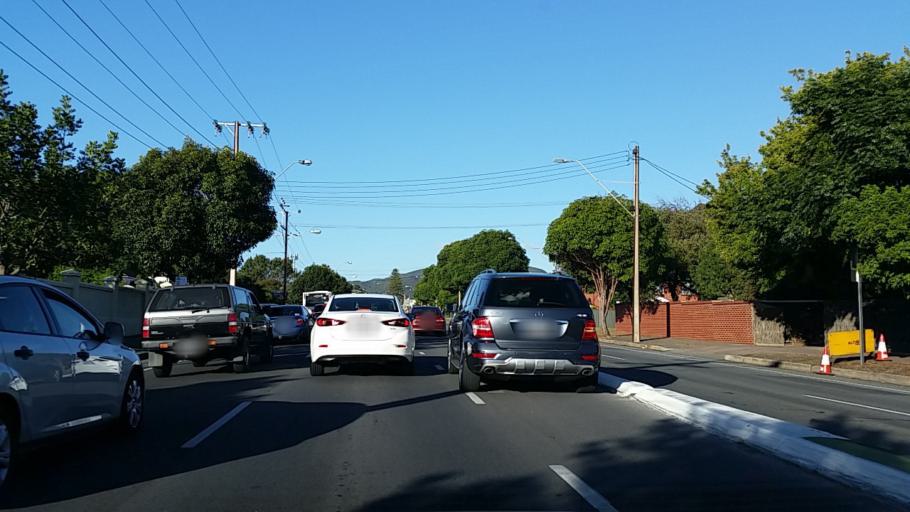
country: AU
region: South Australia
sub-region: Burnside
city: Glenunga
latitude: -34.9394
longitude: 138.6382
